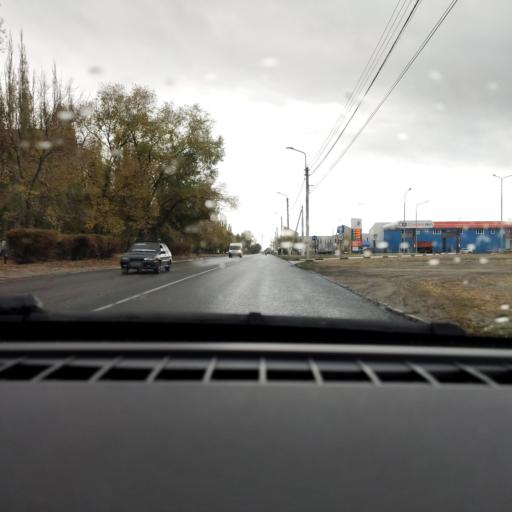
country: RU
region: Voronezj
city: Maslovka
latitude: 51.6000
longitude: 39.2368
